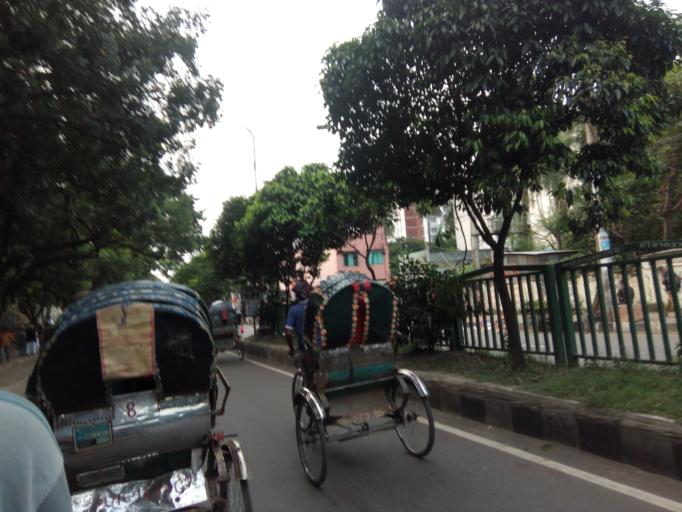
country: BD
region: Dhaka
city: Azimpur
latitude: 23.7257
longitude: 90.3866
